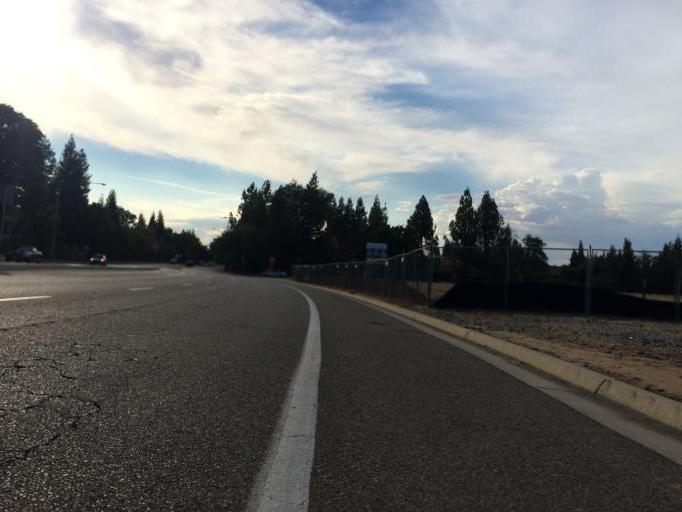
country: US
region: California
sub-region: Fresno County
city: Clovis
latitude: 36.8688
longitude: -119.7577
